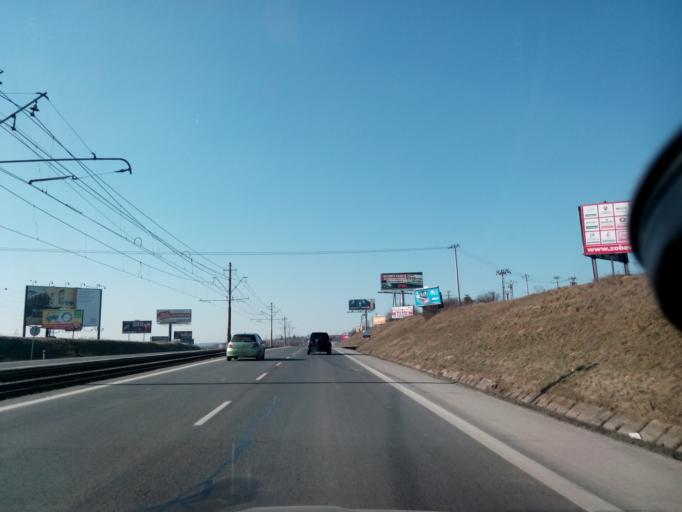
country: SK
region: Kosicky
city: Kosice
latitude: 48.6901
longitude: 21.2270
